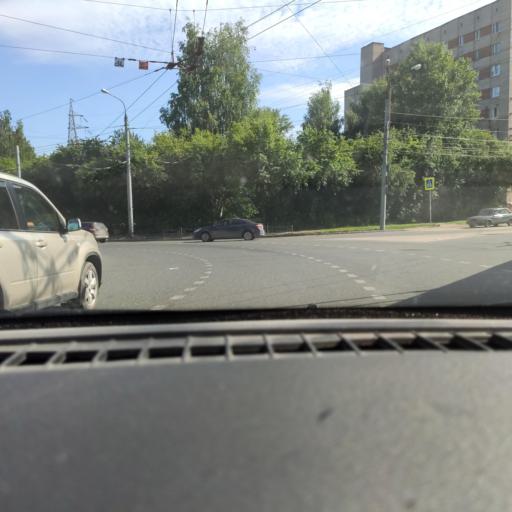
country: RU
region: Udmurtiya
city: Izhevsk
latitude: 56.8777
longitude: 53.2584
